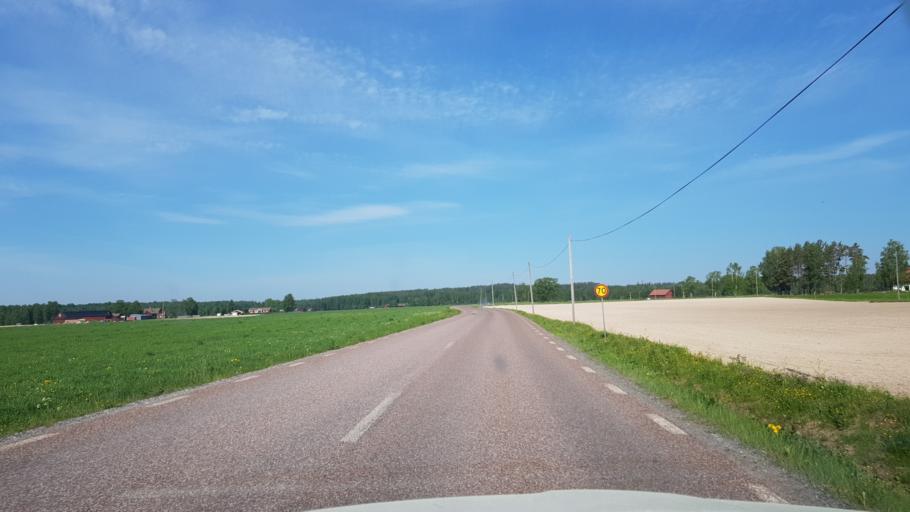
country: SE
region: Dalarna
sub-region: Saters Kommun
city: Saeter
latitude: 60.4153
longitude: 15.7234
